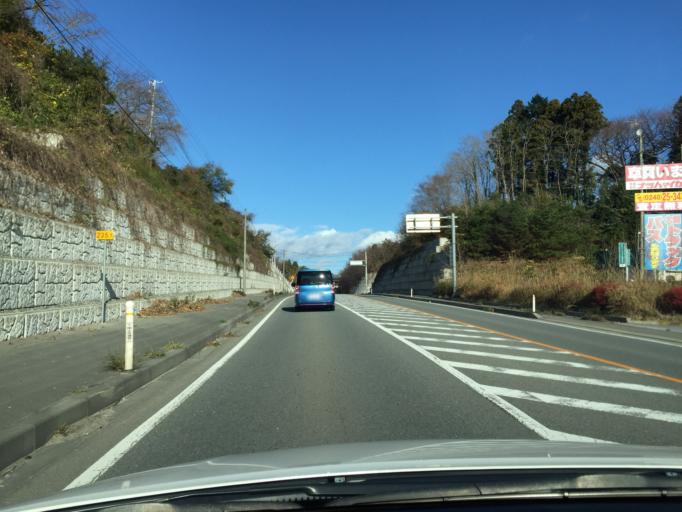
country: JP
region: Fukushima
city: Namie
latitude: 37.2839
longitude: 140.9918
